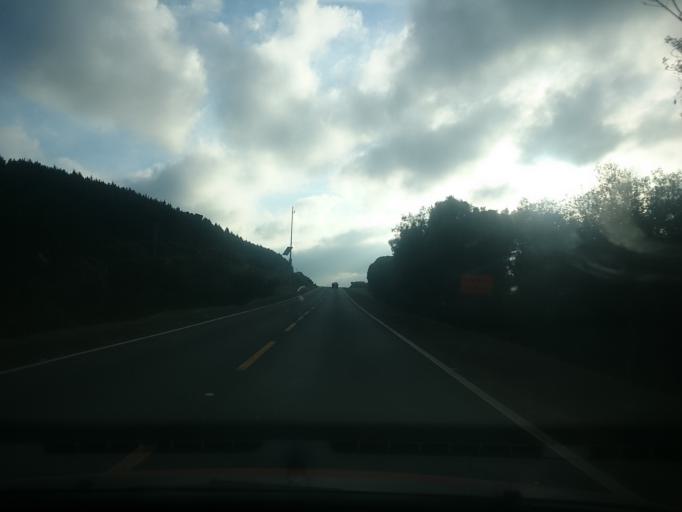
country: BR
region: Santa Catarina
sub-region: Lages
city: Lages
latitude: -27.9984
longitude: -50.5323
